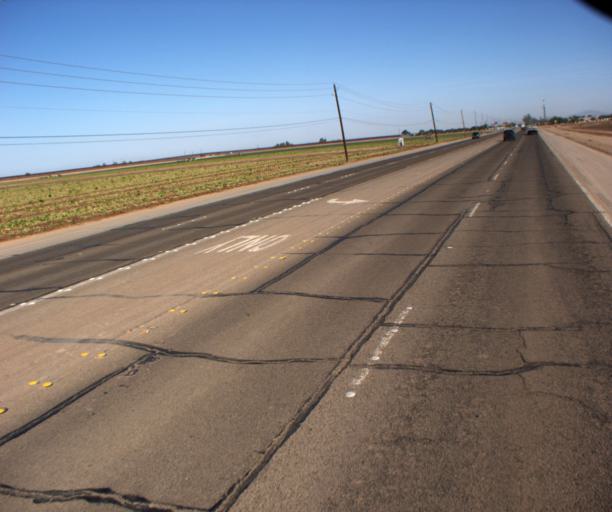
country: US
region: Arizona
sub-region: Yuma County
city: San Luis
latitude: 32.5381
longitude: -114.7868
